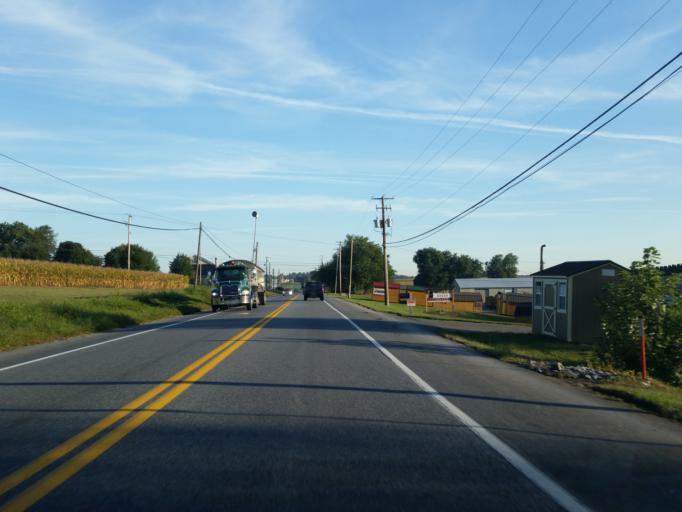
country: US
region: Pennsylvania
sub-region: Lancaster County
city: Quarryville
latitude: 39.7991
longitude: -76.1852
